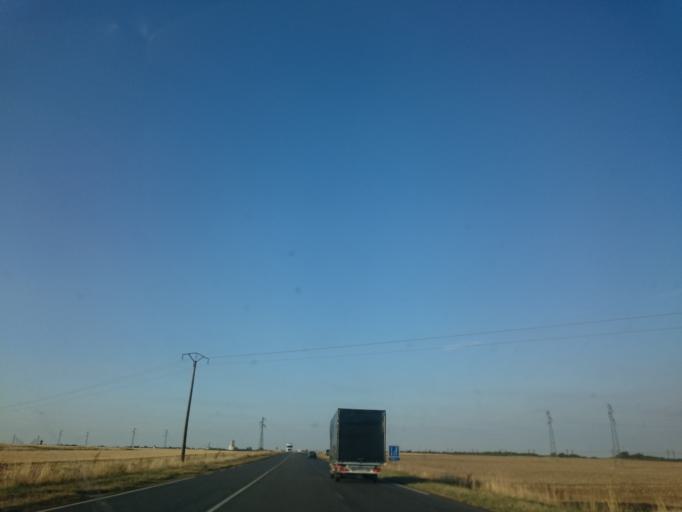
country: FR
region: Centre
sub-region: Departement d'Eure-et-Loir
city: Toury
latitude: 48.1695
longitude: 1.9198
